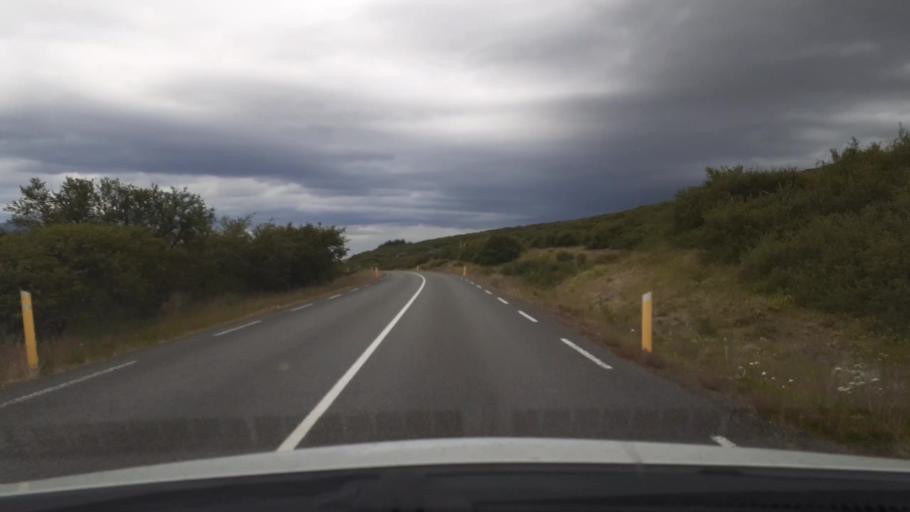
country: IS
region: West
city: Borgarnes
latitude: 64.5428
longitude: -21.5599
